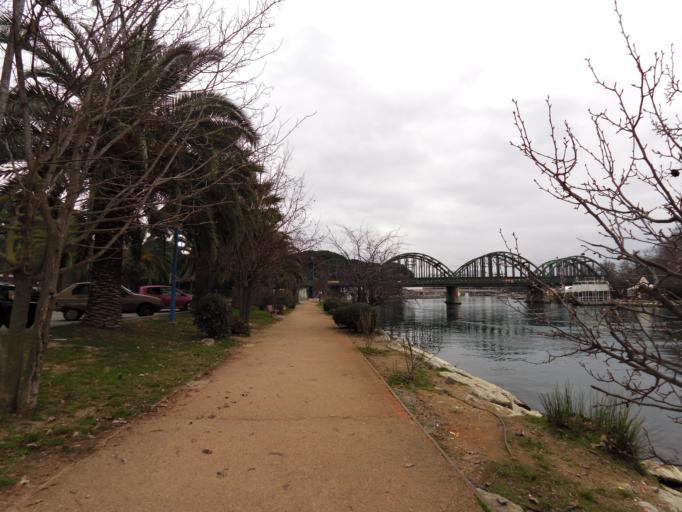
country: FR
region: Provence-Alpes-Cote d'Azur
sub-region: Departement des Alpes-Maritimes
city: Mandelieu-la-Napoule
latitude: 43.5337
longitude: 6.9455
